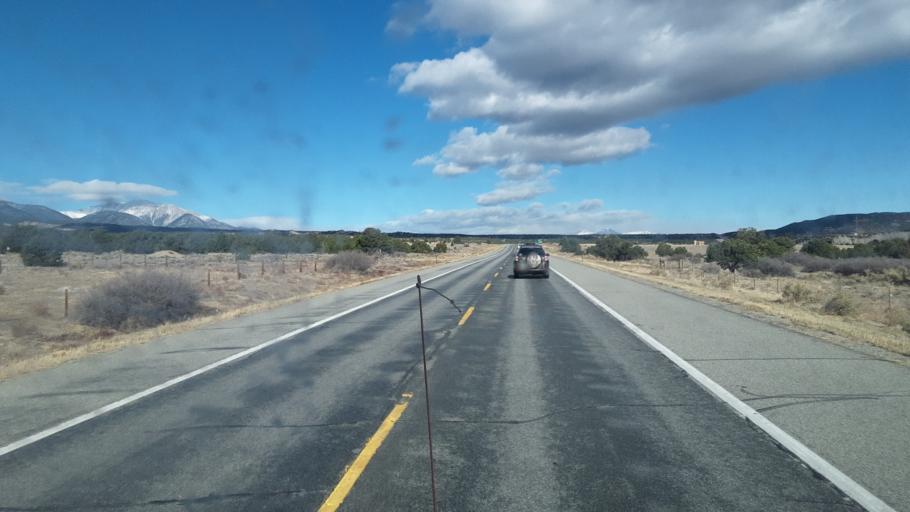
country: US
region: Colorado
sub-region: Chaffee County
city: Salida
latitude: 38.5864
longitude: -106.0835
